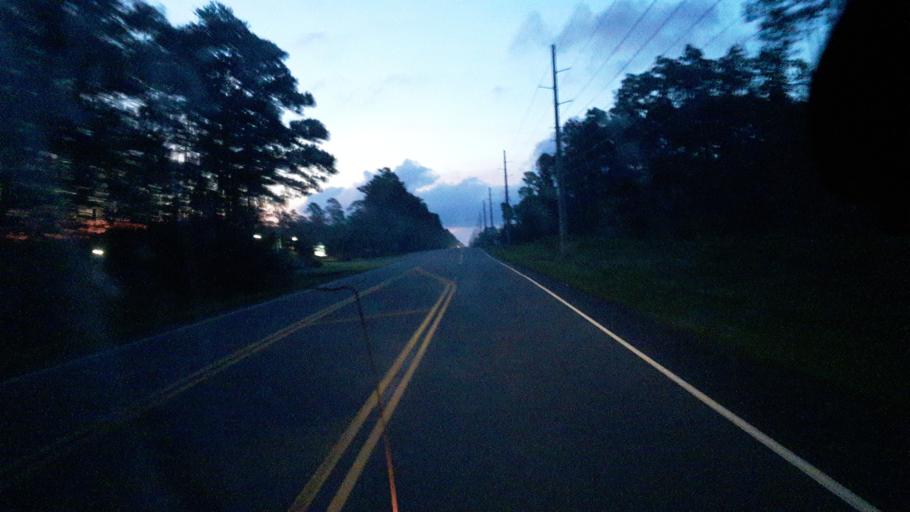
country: US
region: North Carolina
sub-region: Brunswick County
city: Oak Island
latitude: 33.9934
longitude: -78.2203
